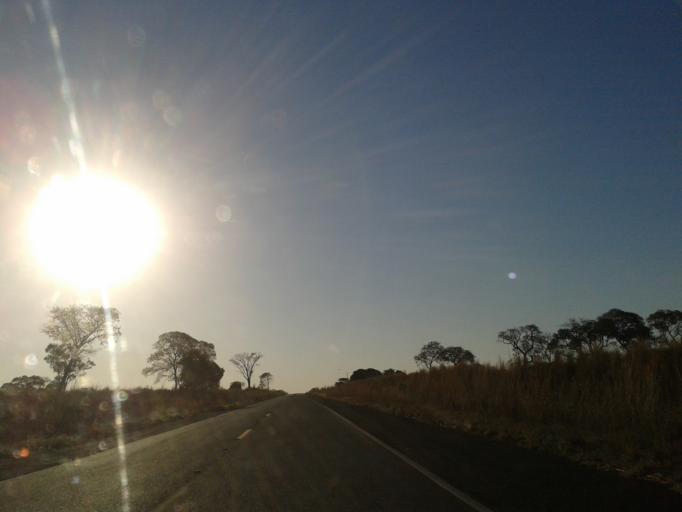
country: BR
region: Minas Gerais
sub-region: Santa Vitoria
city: Santa Vitoria
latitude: -19.0942
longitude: -50.3406
